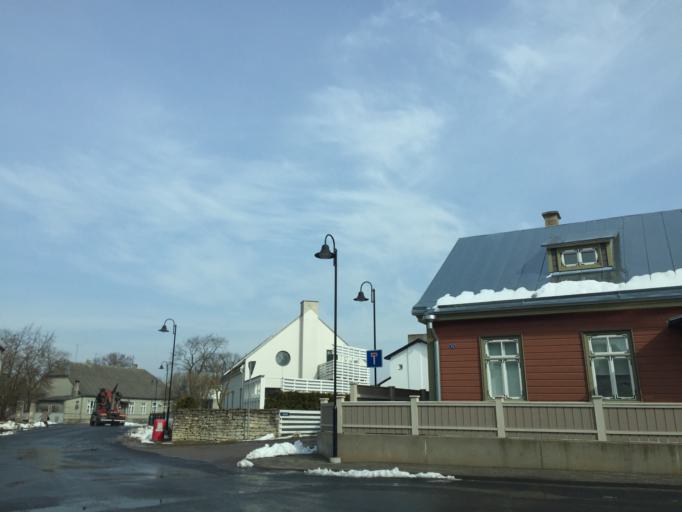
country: EE
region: Saare
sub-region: Kuressaare linn
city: Kuressaare
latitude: 58.2496
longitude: 22.4765
